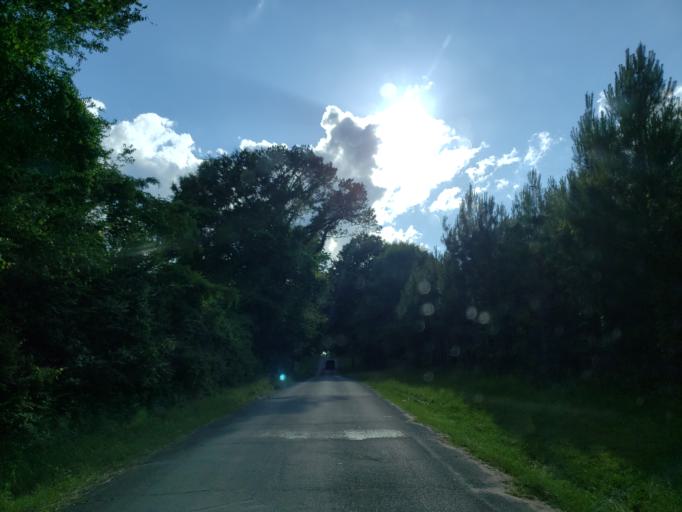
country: US
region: Mississippi
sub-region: Forrest County
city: Petal
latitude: 31.3176
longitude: -89.1987
